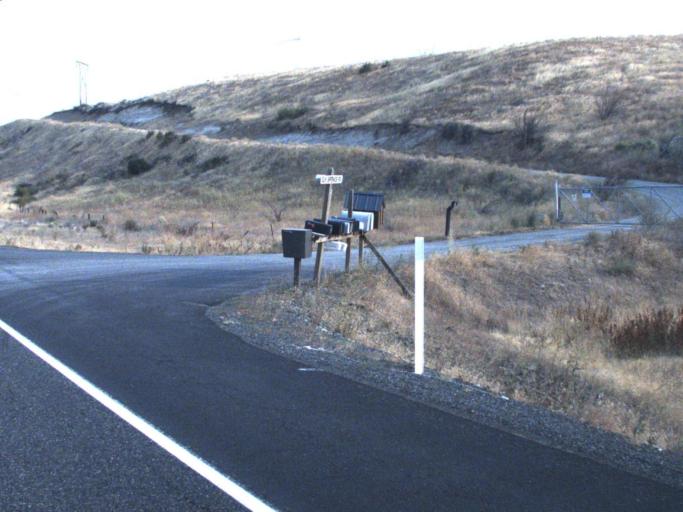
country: US
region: Washington
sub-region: Kittitas County
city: Ellensburg
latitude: 47.1343
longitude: -120.6865
